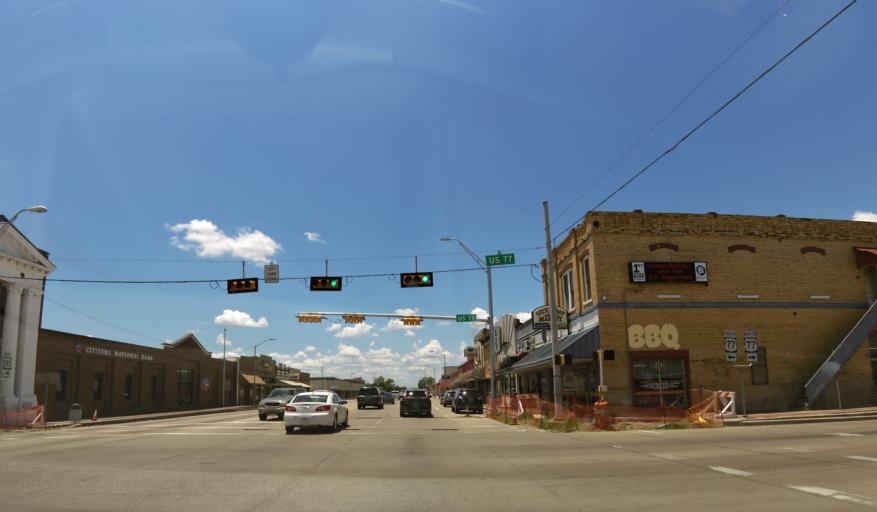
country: US
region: Texas
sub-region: Lee County
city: Giddings
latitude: 30.1829
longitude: -96.9372
